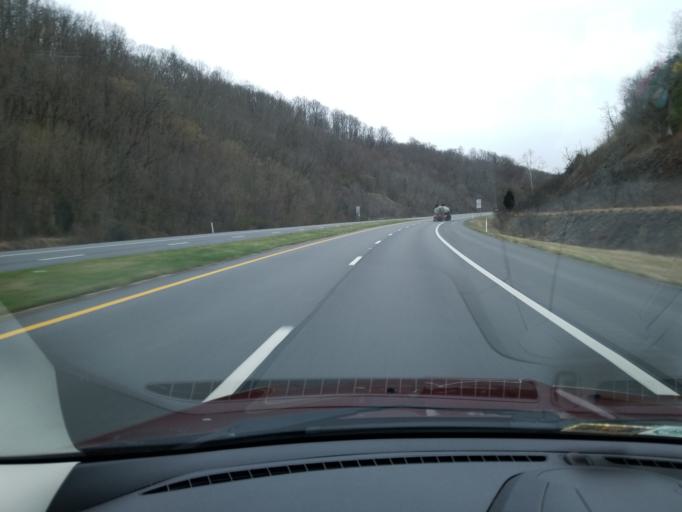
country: US
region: Virginia
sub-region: Giles County
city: Narrows
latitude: 37.3652
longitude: -80.8700
